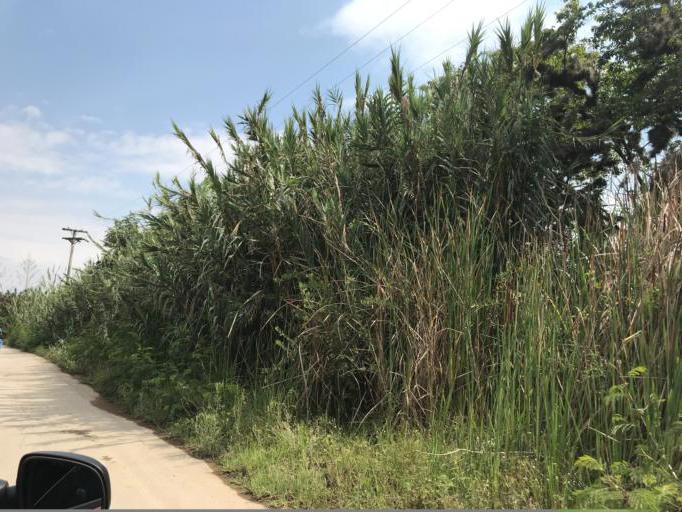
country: CO
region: Boyaca
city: Villa de Leiva
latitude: 5.6585
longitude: -73.5810
